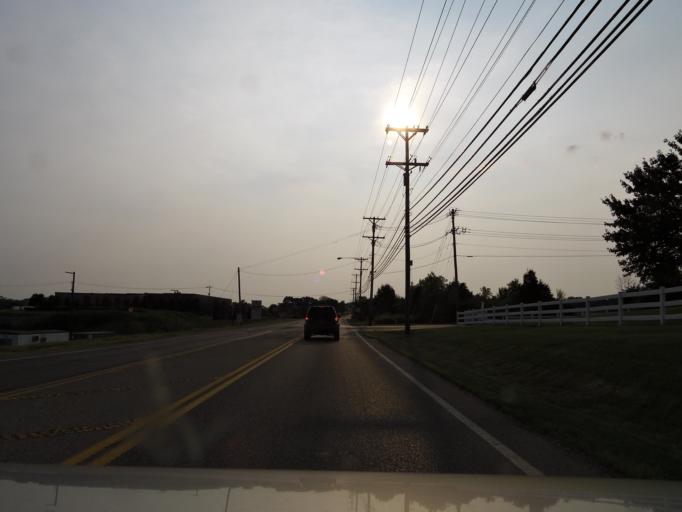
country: US
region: Ohio
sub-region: Butler County
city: Hamilton
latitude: 39.3791
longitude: -84.5152
